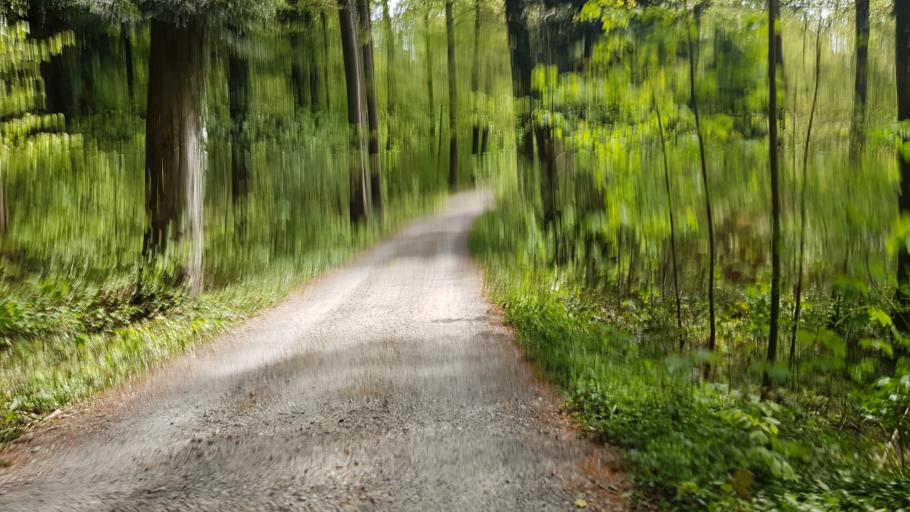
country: CH
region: Aargau
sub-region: Bezirk Kulm
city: Reinach
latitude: 47.2722
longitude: 8.1794
